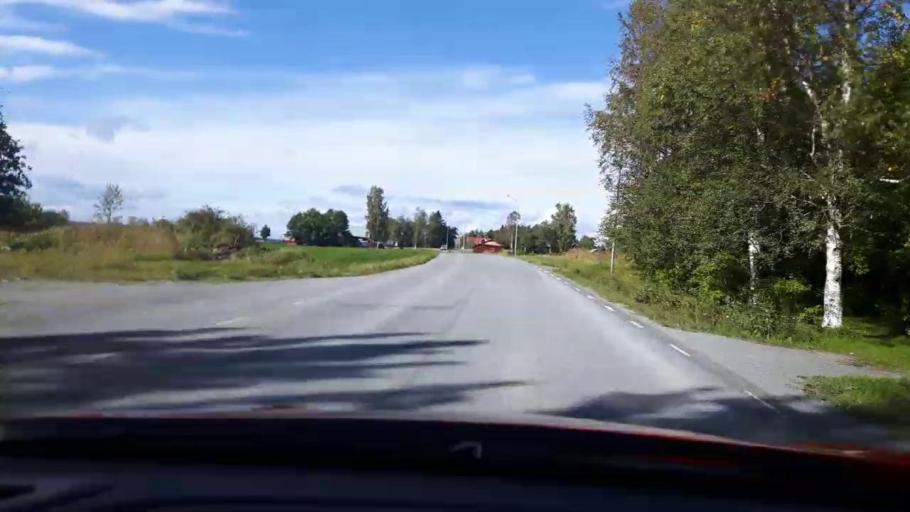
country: SE
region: Jaemtland
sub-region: OEstersunds Kommun
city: Ostersund
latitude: 63.0449
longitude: 14.4555
